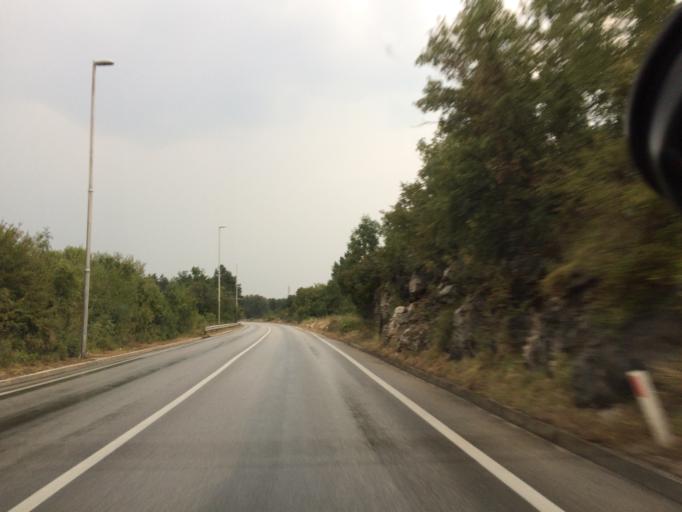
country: ME
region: Opstina Niksic
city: Niksic
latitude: 42.7776
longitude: 18.9363
